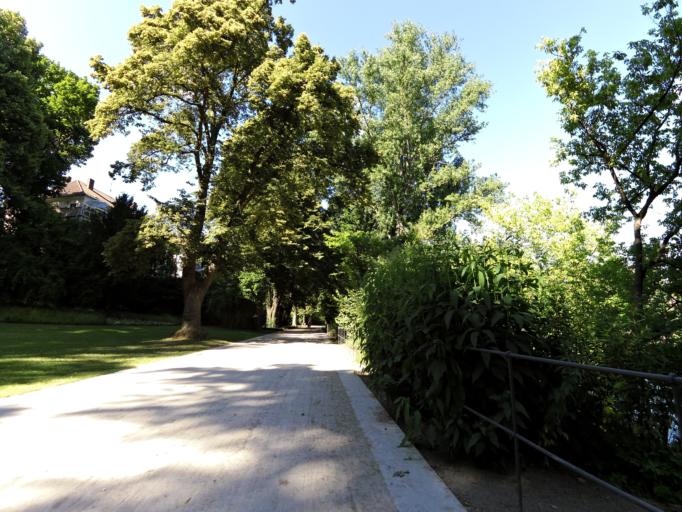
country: DE
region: Rheinland-Pfalz
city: Koblenz
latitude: 50.3408
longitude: 7.5872
